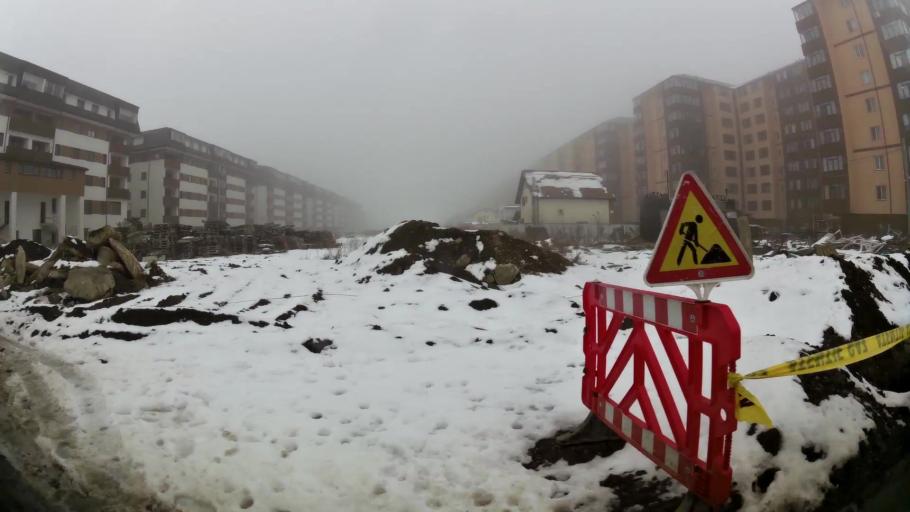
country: RO
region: Ilfov
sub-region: Comuna Chiajna
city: Chiajna
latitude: 44.4477
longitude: 25.9758
